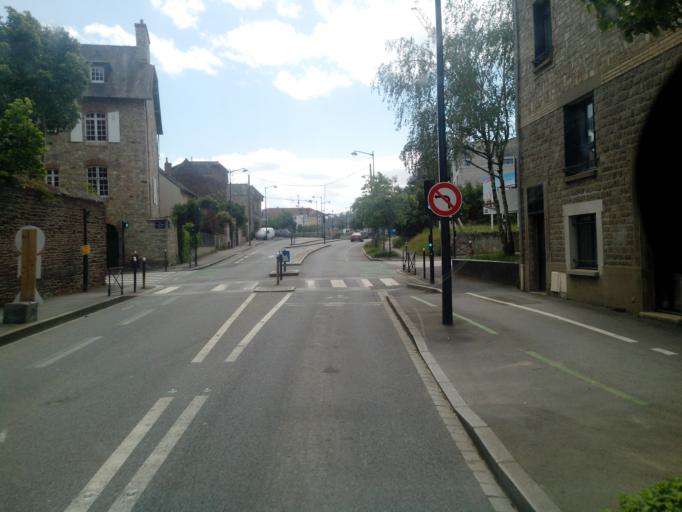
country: FR
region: Brittany
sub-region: Departement d'Ille-et-Vilaine
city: Rennes
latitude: 48.1040
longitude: -1.6939
